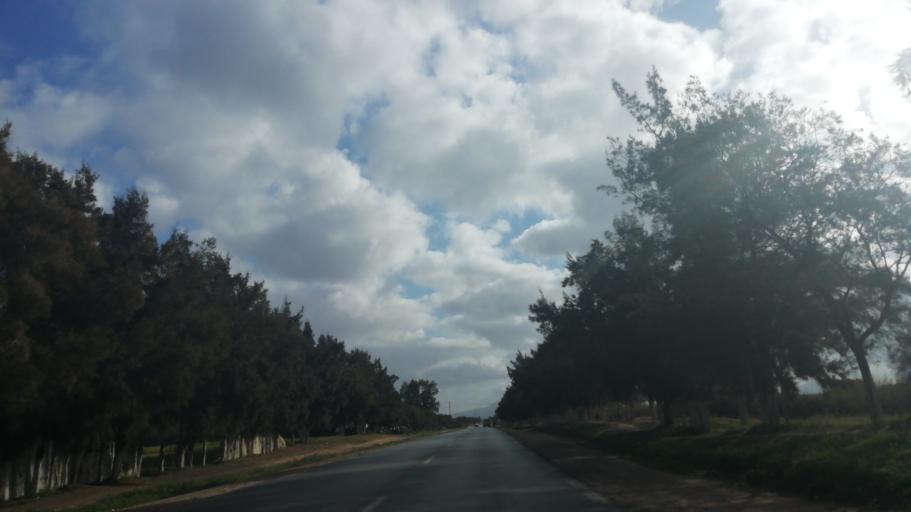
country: DZ
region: Relizane
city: Mazouna
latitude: 36.2562
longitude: 0.5858
